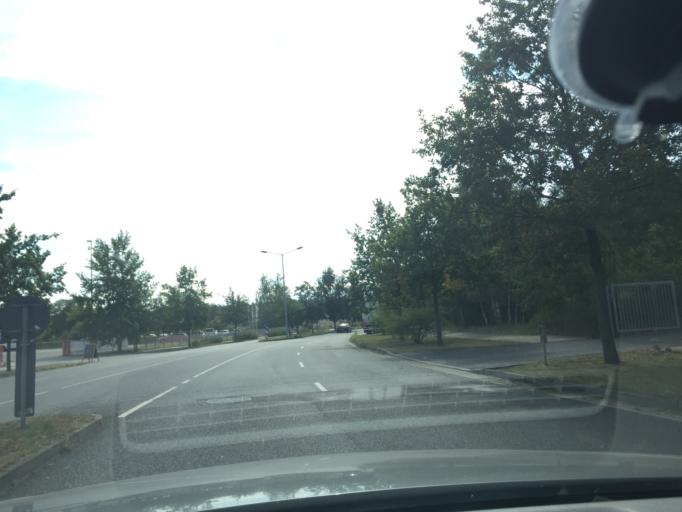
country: DE
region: Brandenburg
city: Grunheide
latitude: 52.3861
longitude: 13.8001
